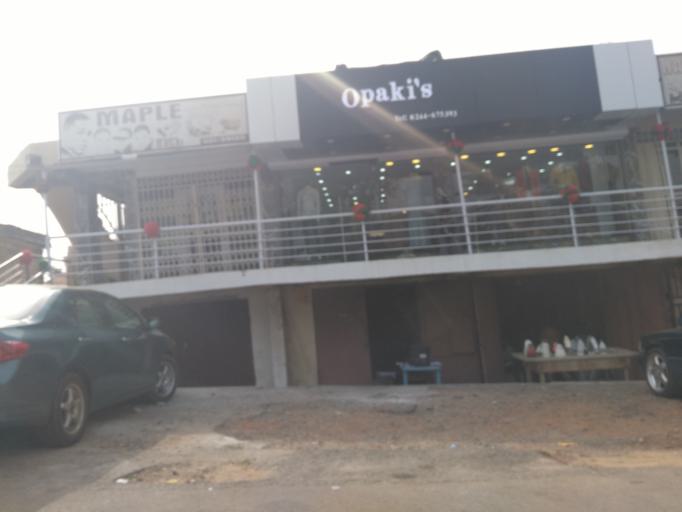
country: GH
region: Ashanti
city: Kumasi
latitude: 6.6840
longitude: -1.6081
